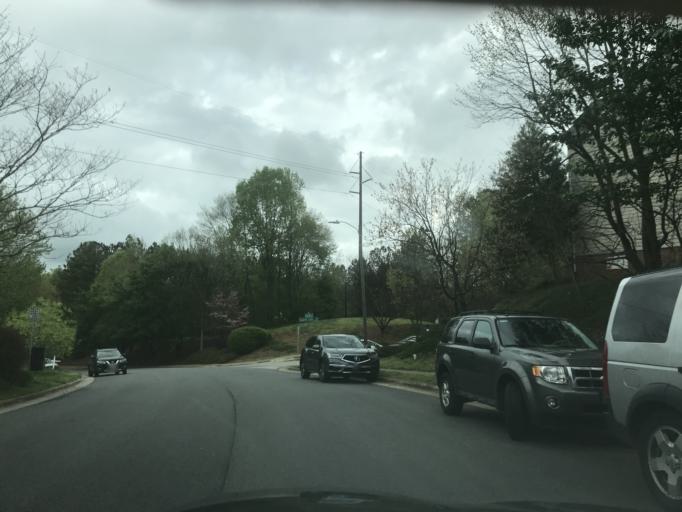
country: US
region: North Carolina
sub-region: Wake County
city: West Raleigh
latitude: 35.7491
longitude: -78.6852
